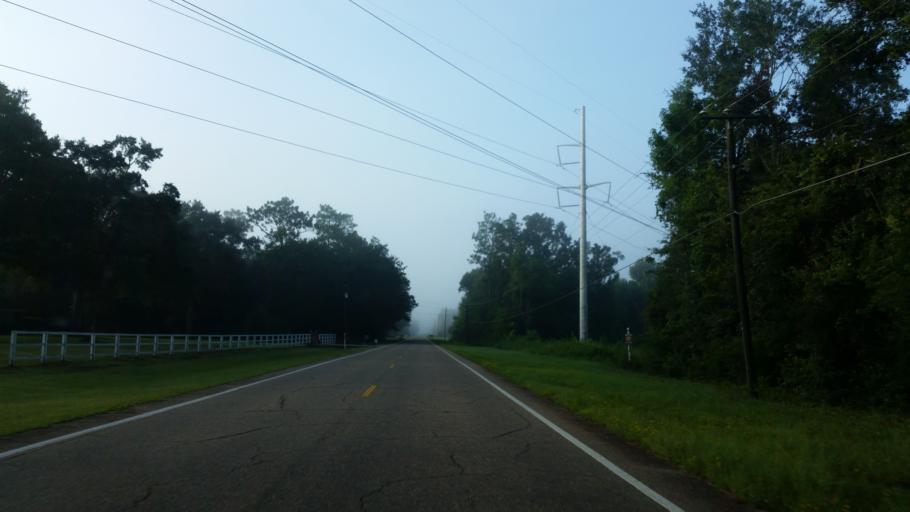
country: US
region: Florida
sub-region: Escambia County
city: Molino
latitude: 30.7374
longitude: -87.3475
